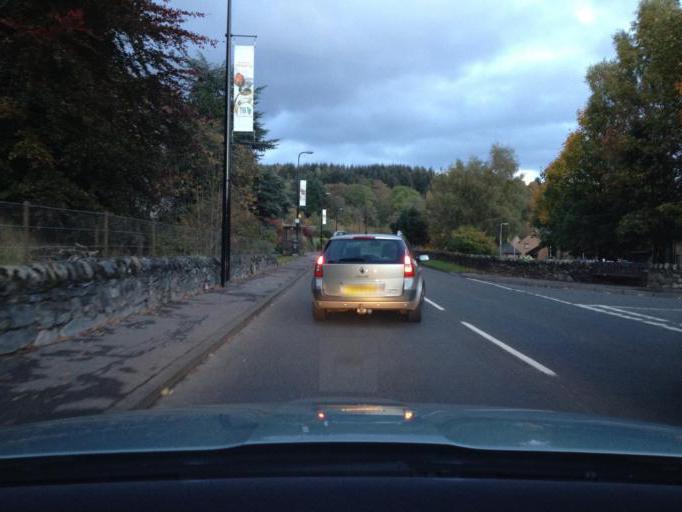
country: GB
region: Scotland
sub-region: Perth and Kinross
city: Pitlochry
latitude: 56.6974
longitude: -3.7197
